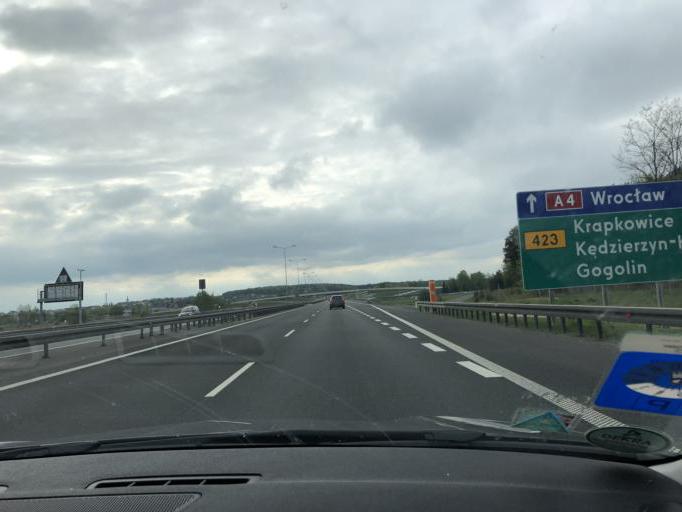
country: PL
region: Opole Voivodeship
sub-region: Powiat krapkowicki
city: Gogolin
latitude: 50.4856
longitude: 18.0008
